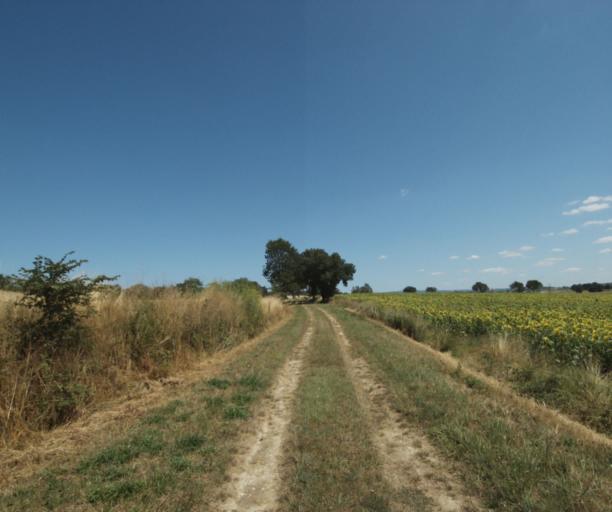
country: FR
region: Midi-Pyrenees
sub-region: Departement de la Haute-Garonne
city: Saint-Felix-Lauragais
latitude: 43.4974
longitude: 1.8715
